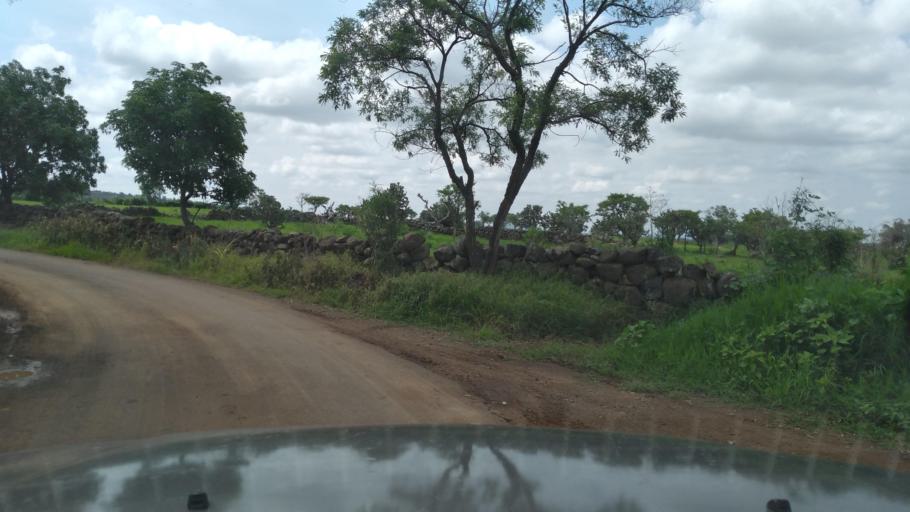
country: MX
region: Jalisco
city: Capilla de Guadalupe
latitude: 20.7482
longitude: -102.6287
